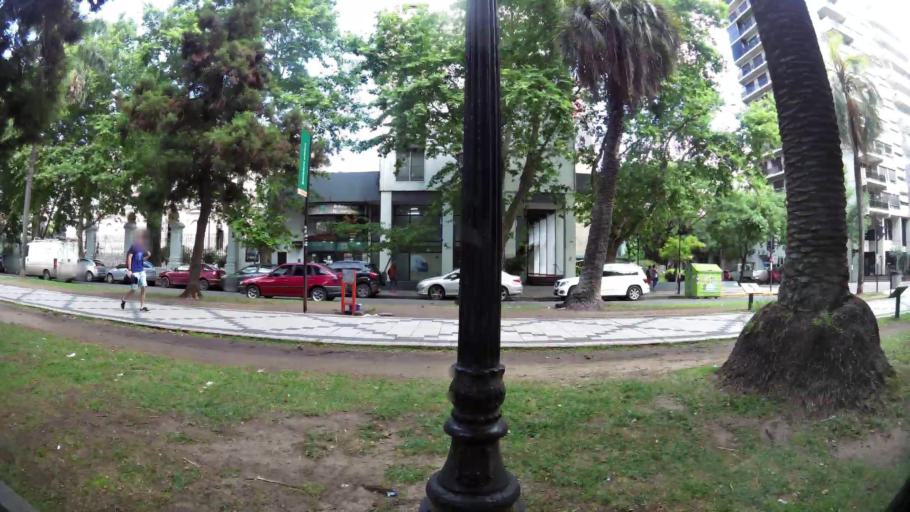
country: AR
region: Santa Fe
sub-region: Departamento de Rosario
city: Rosario
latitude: -32.9451
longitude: -60.6536
